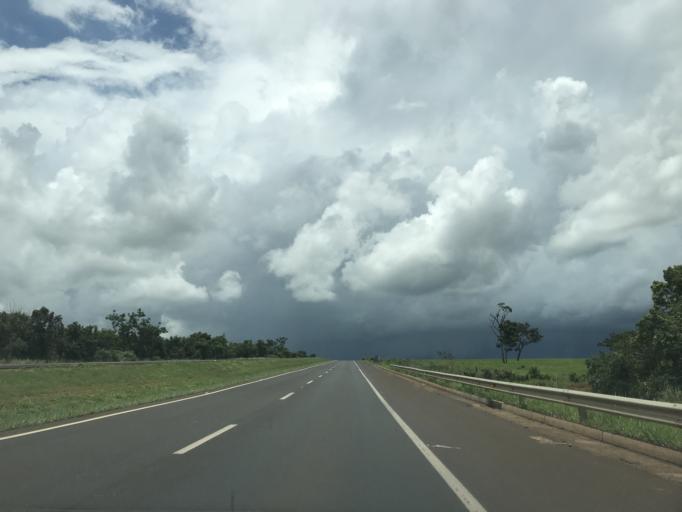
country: BR
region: Minas Gerais
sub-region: Prata
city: Prata
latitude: -19.4536
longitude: -48.8835
